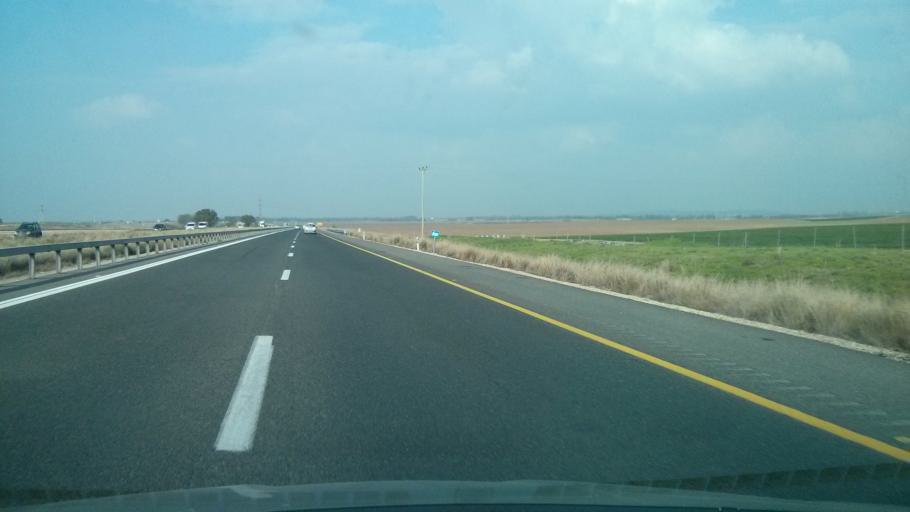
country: IL
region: Central District
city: Gedera
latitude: 31.7651
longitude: 34.8285
